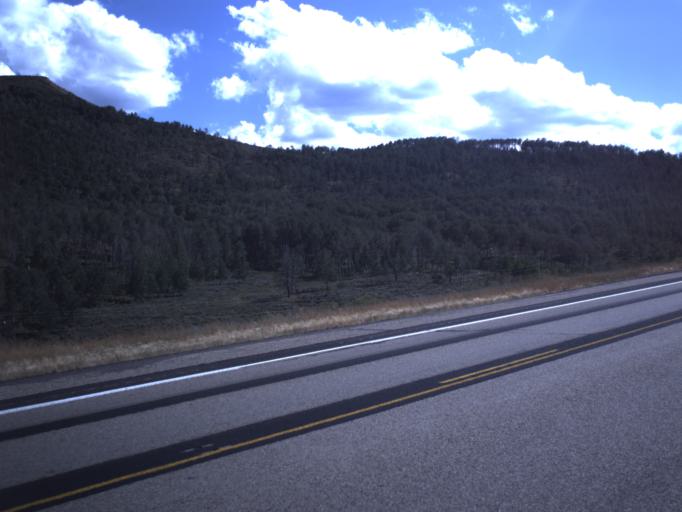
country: US
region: Utah
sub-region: Summit County
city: Francis
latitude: 40.1894
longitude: -111.0173
